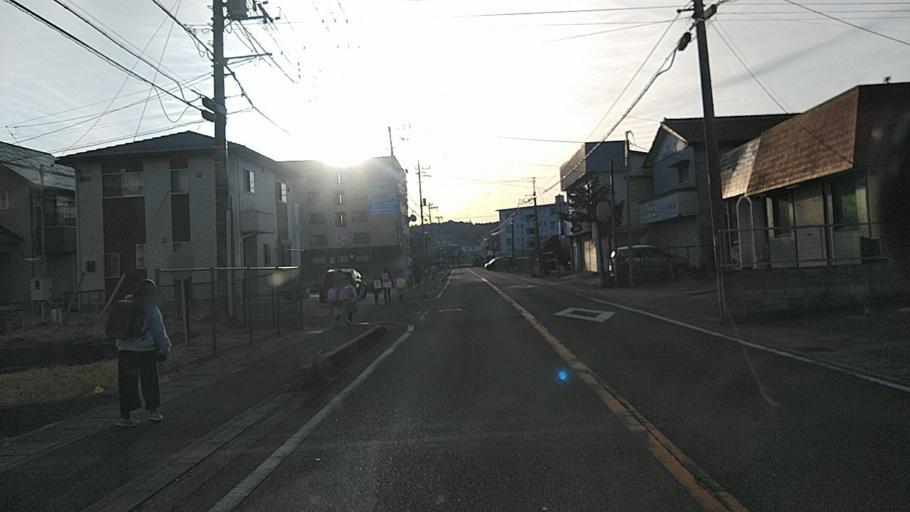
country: JP
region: Chiba
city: Kimitsu
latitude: 35.3067
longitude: 139.9232
